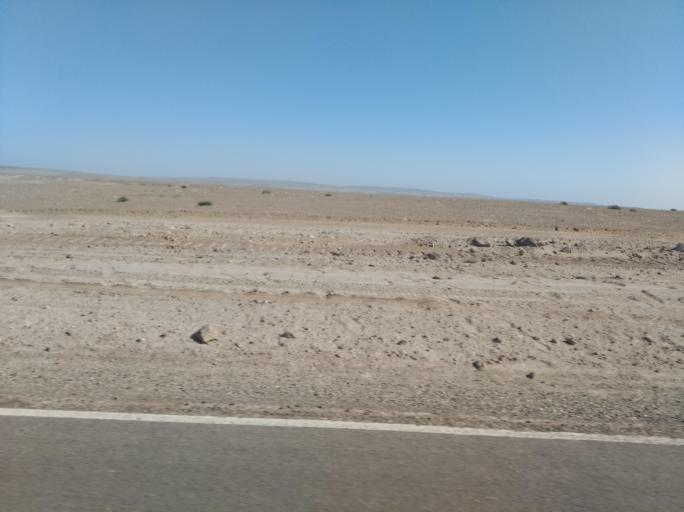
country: CL
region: Atacama
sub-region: Provincia de Copiapo
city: Copiapo
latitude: -27.3168
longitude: -70.8358
